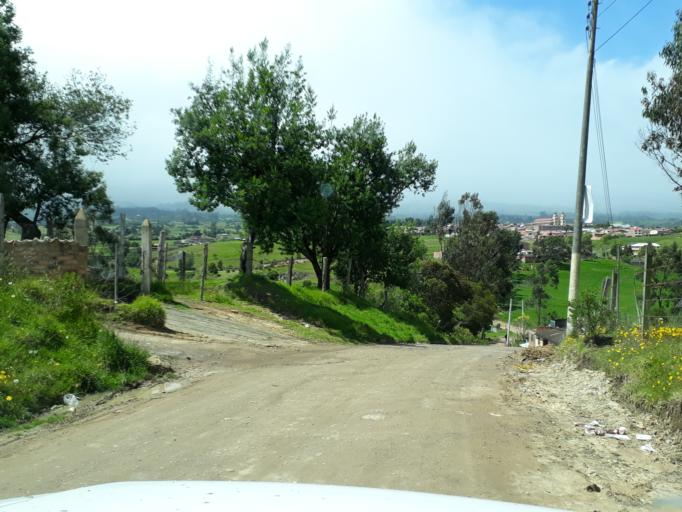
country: CO
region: Cundinamarca
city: Guasca
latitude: 4.8757
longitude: -73.8804
